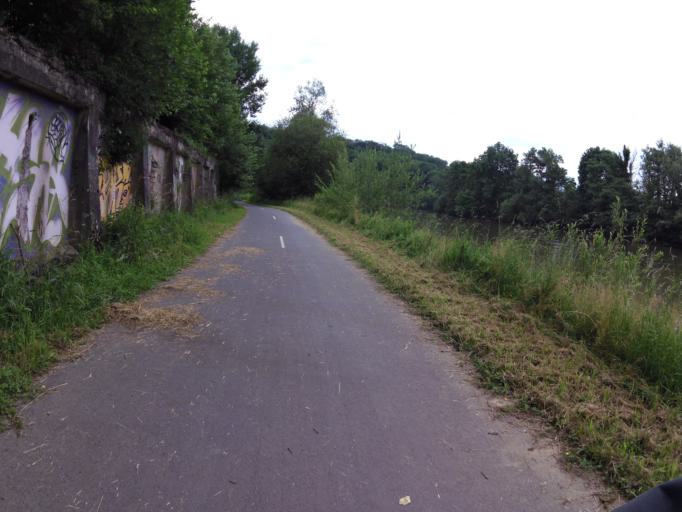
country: FR
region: Champagne-Ardenne
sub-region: Departement des Ardennes
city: Donchery
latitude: 49.7018
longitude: 4.8978
